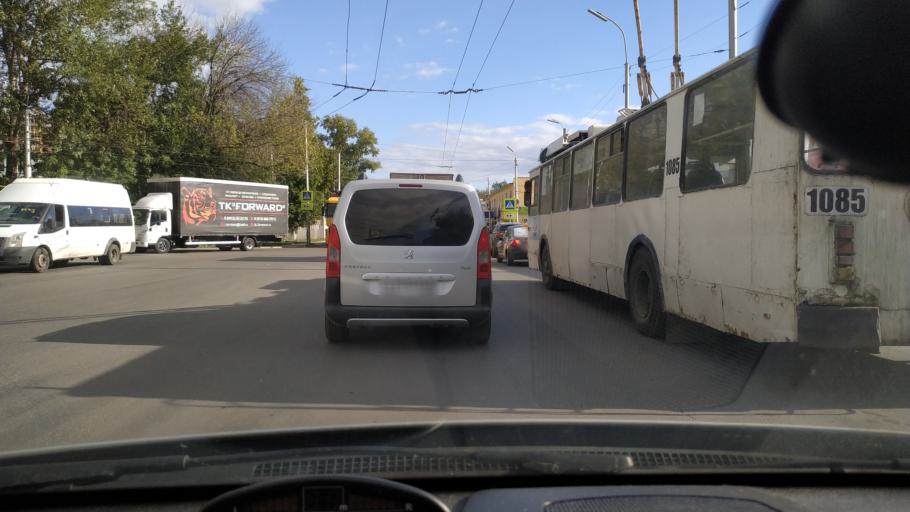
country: RU
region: Rjazan
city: Ryazan'
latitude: 54.6156
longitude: 39.6937
